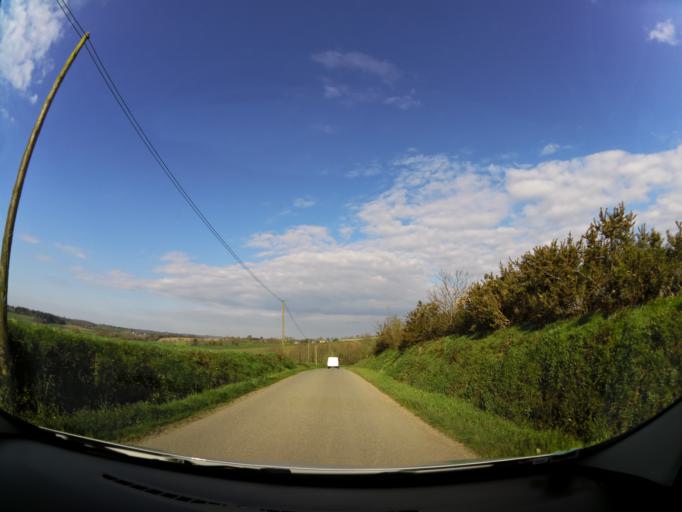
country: FR
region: Brittany
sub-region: Departement d'Ille-et-Vilaine
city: Crevin
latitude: 47.9401
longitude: -1.6851
